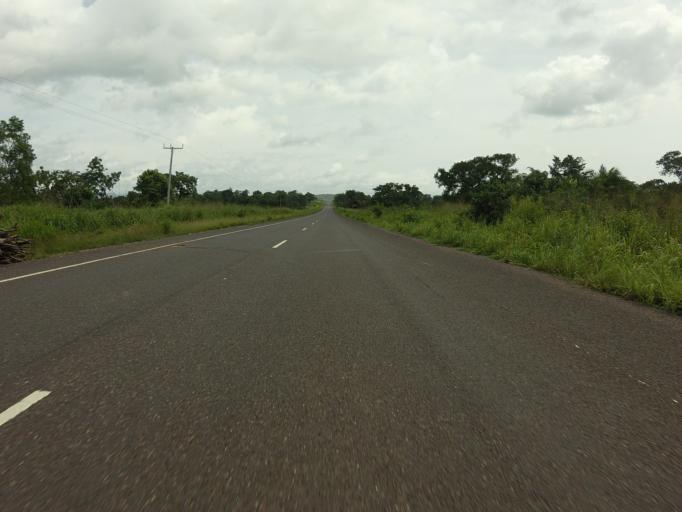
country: TG
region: Plateaux
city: Badou
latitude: 7.9742
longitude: 0.5592
